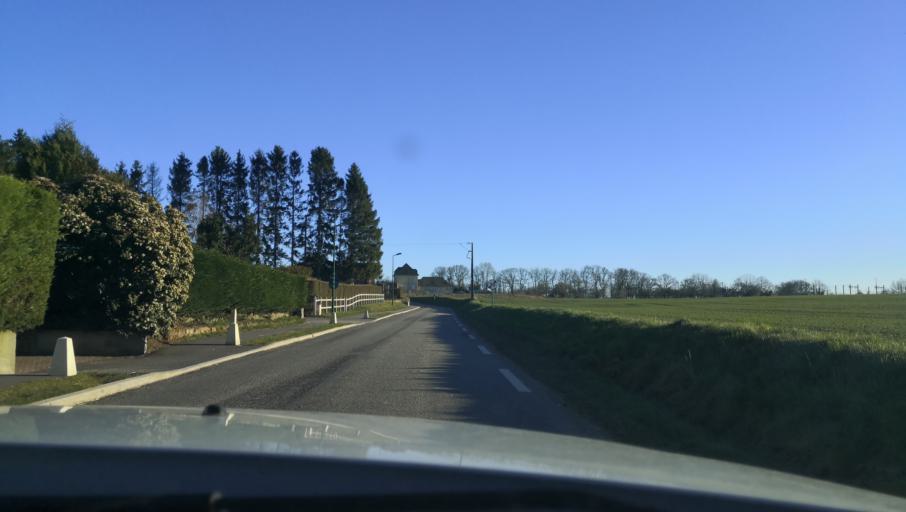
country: FR
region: Haute-Normandie
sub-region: Departement de la Seine-Maritime
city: Buchy
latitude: 49.6055
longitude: 1.3310
